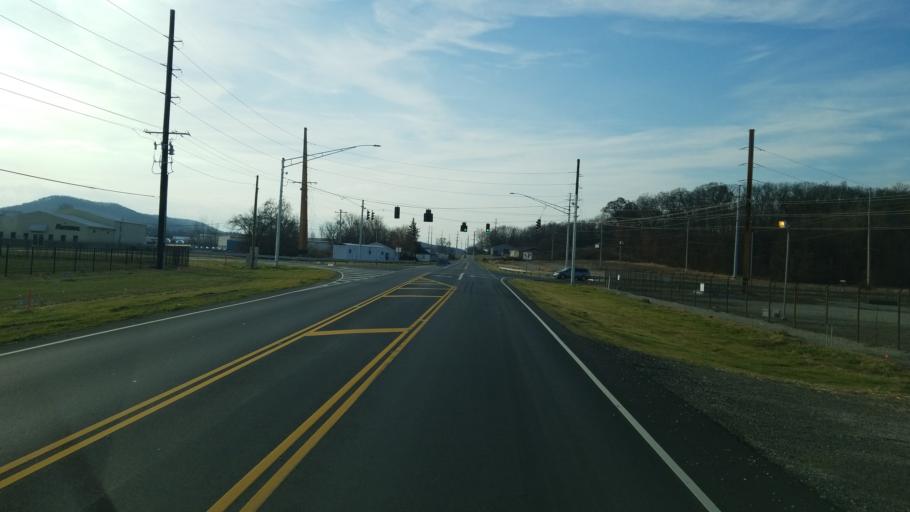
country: US
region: Ohio
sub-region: Ross County
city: Chillicothe
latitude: 39.4080
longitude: -82.9595
